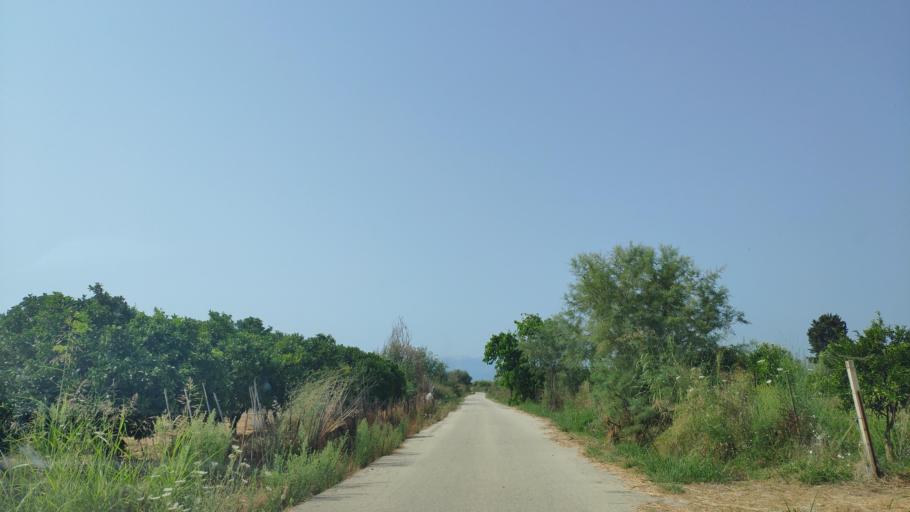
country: GR
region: Epirus
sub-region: Nomos Artas
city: Kompoti
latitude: 39.0587
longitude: 21.0725
